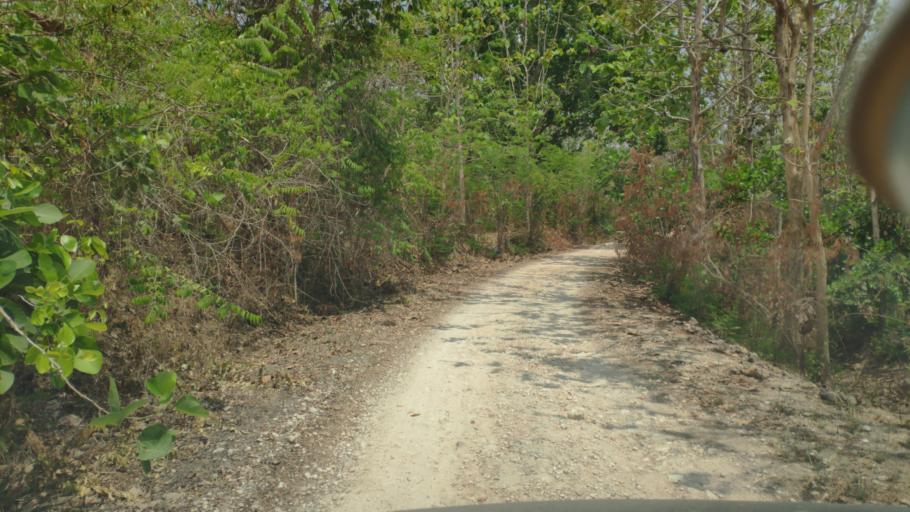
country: ID
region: Central Java
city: Suruhan
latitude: -6.9960
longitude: 111.5208
